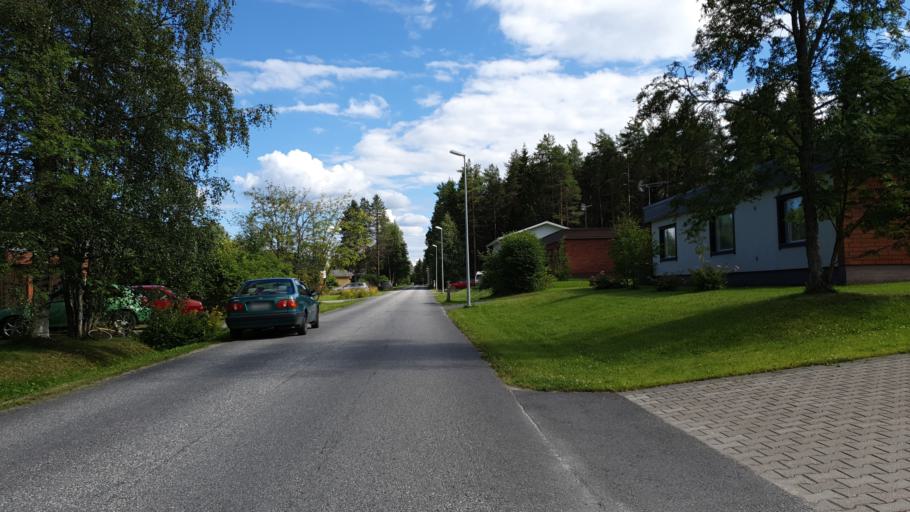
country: FI
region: Kainuu
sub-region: Kehys-Kainuu
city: Kuhmo
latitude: 64.1180
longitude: 29.5040
